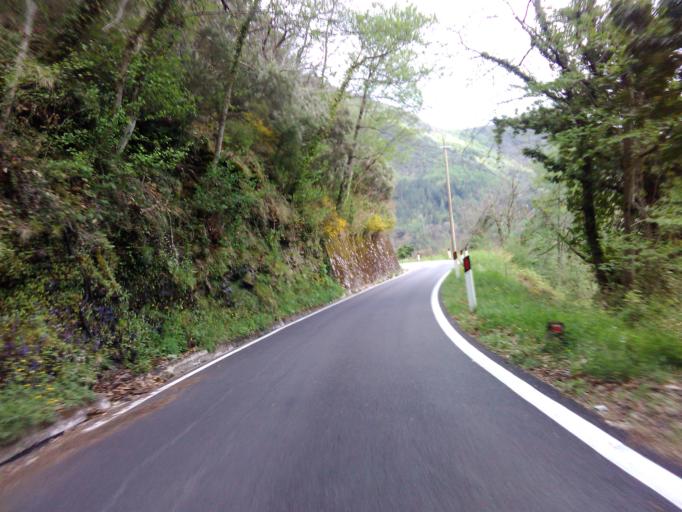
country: IT
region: Tuscany
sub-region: Provincia di Lucca
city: Pontestazzemese
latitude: 43.9736
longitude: 10.2789
